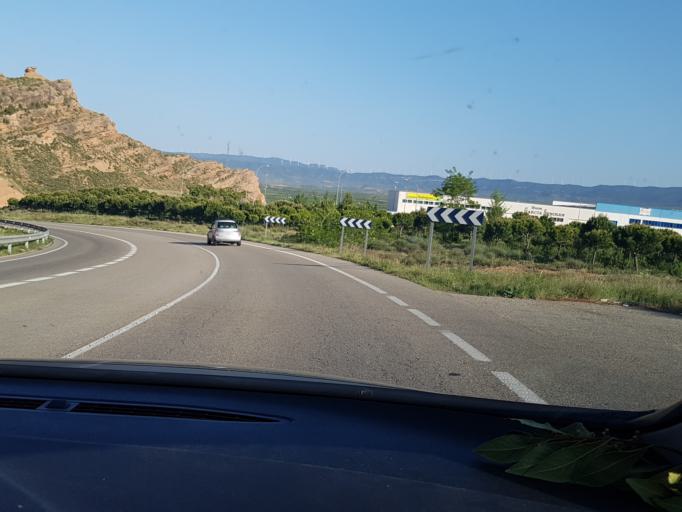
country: ES
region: La Rioja
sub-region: Provincia de La Rioja
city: Arnedo
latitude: 42.2367
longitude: -2.0849
